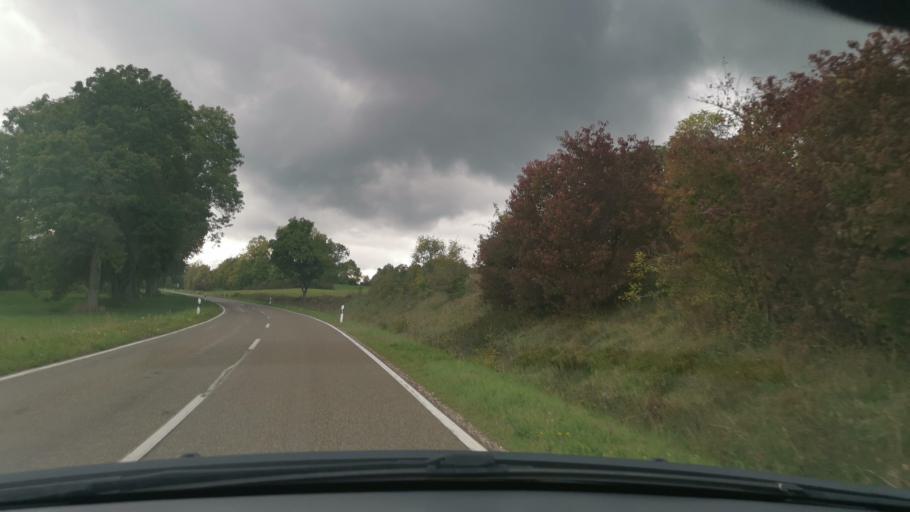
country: DE
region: Baden-Wuerttemberg
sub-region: Tuebingen Region
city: Lauterach
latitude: 48.3119
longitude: 9.5658
